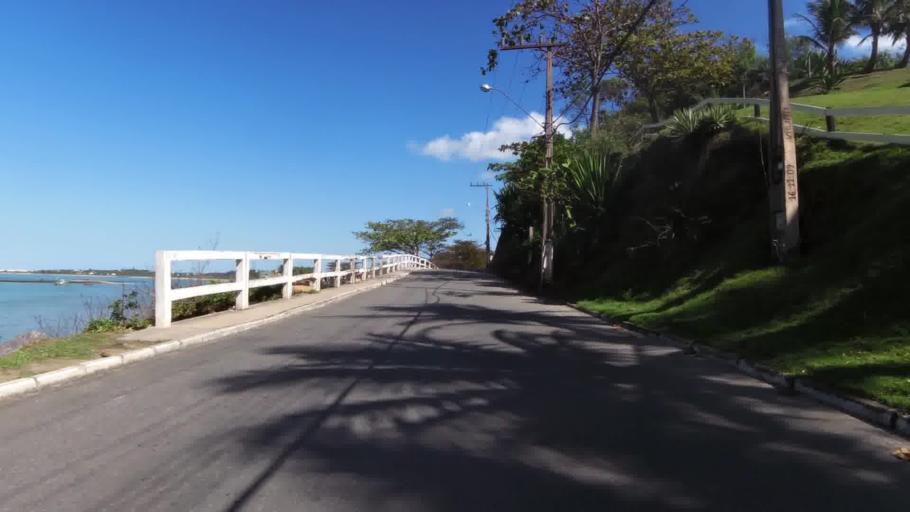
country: BR
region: Espirito Santo
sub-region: Piuma
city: Piuma
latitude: -20.8037
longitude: -40.5962
